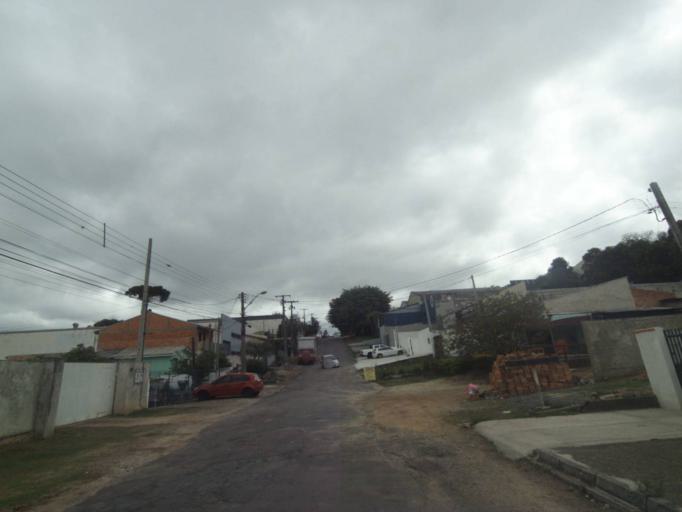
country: BR
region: Parana
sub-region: Pinhais
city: Pinhais
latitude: -25.4025
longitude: -49.2184
